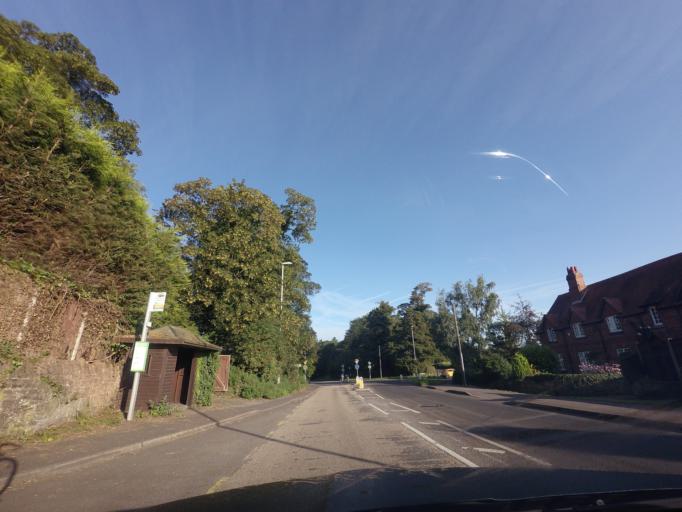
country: GB
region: England
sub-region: Nottinghamshire
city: Kimberley
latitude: 53.0106
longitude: -1.2567
